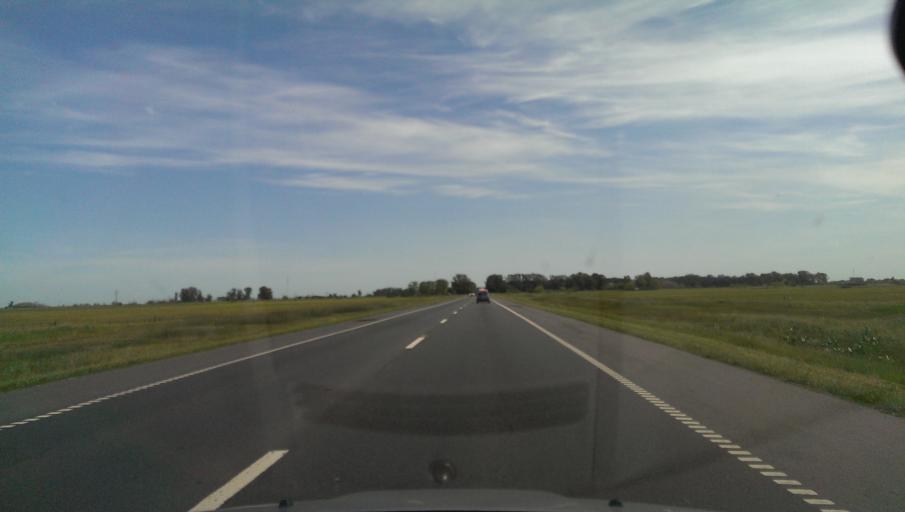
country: AR
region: Buenos Aires
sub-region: Partido de Las Flores
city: Las Flores
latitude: -36.3713
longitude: -59.4703
